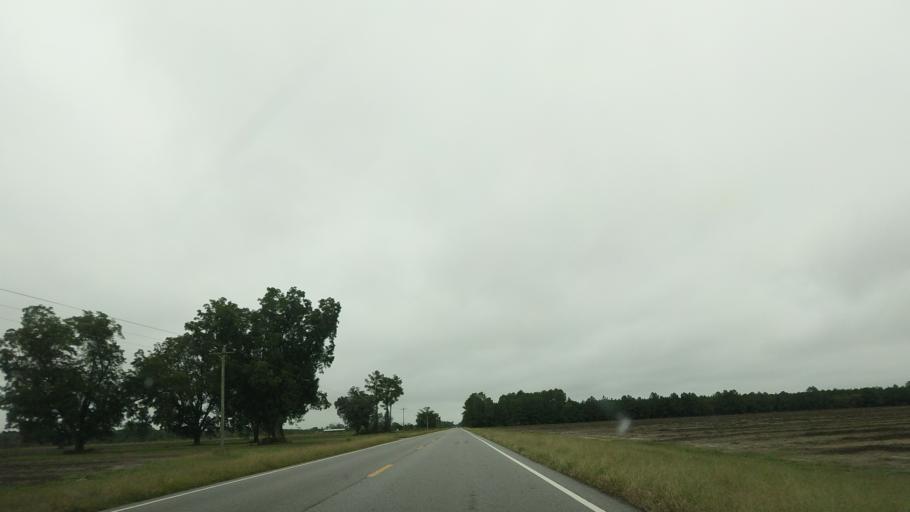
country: US
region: Georgia
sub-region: Berrien County
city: Nashville
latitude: 31.3088
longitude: -83.2324
